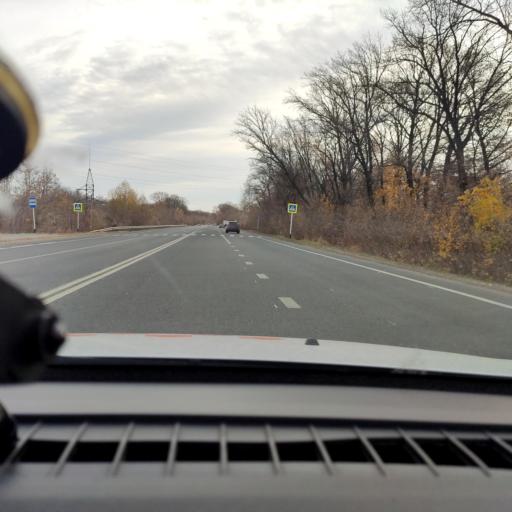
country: RU
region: Samara
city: Novokuybyshevsk
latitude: 53.1443
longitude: 49.9989
